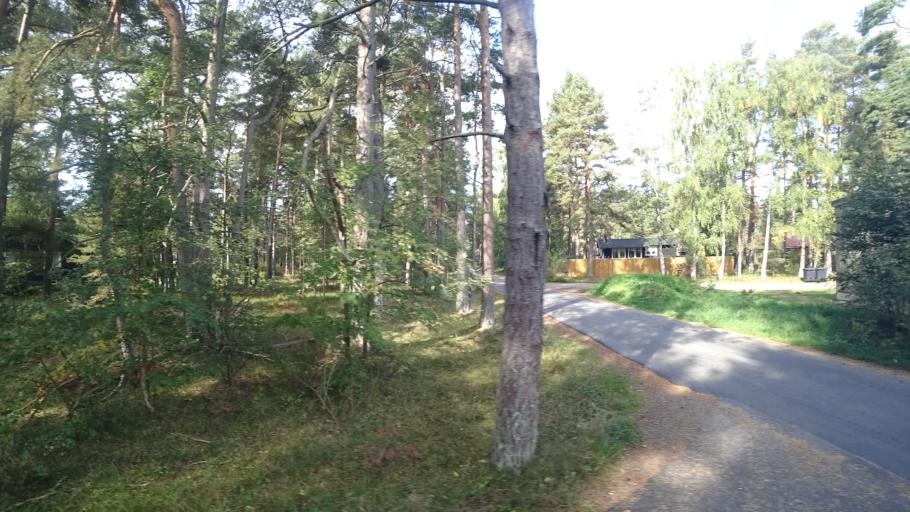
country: SE
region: Skane
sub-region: Kristianstads Kommun
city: Ahus
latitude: 55.9104
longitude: 14.2985
